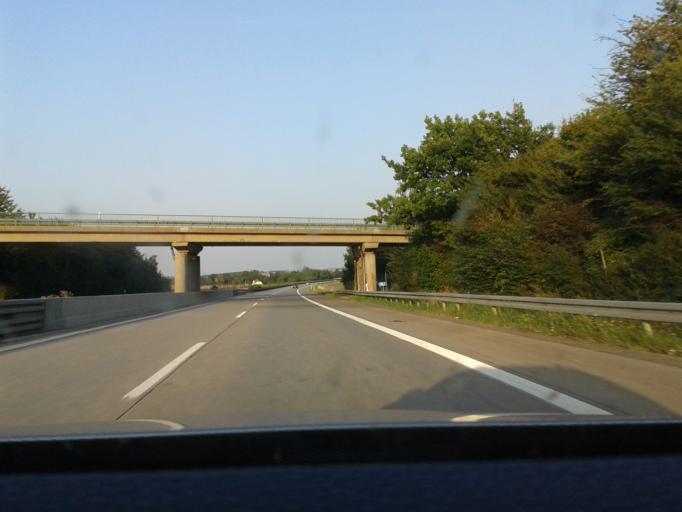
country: DE
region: Saxony
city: Grossweitzschen
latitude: 51.1677
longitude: 13.0708
